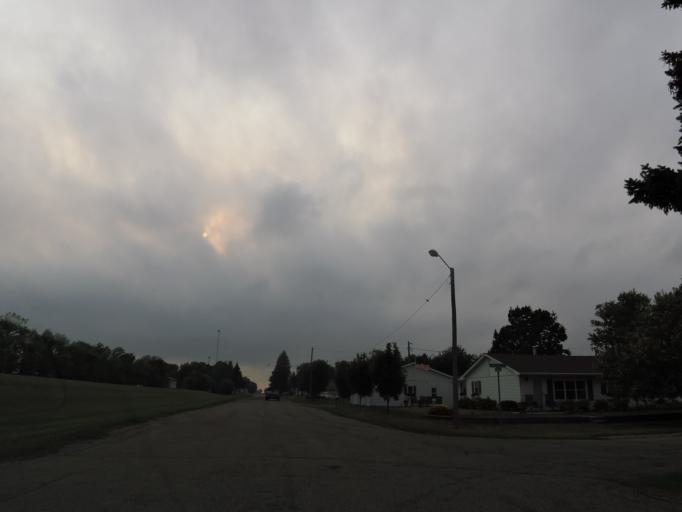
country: US
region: North Dakota
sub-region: Walsh County
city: Grafton
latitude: 48.5568
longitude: -97.1732
